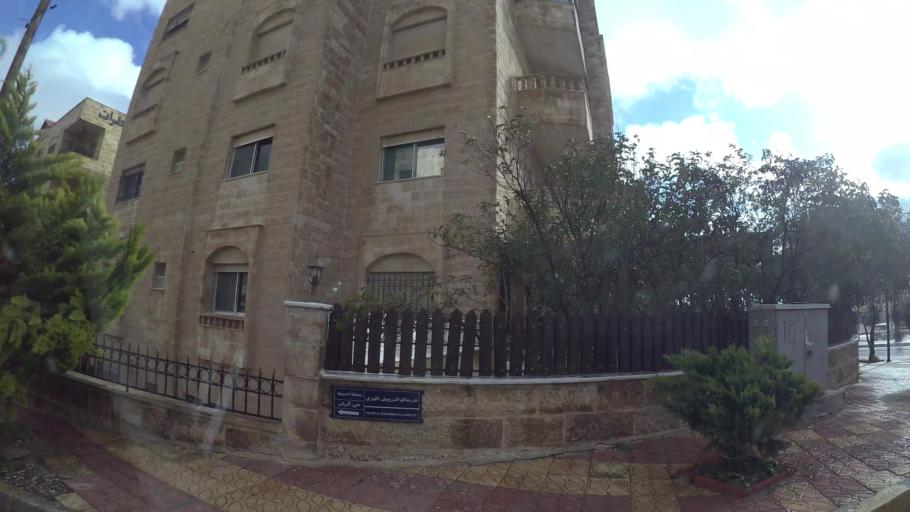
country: JO
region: Amman
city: Al Jubayhah
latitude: 32.0350
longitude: 35.8643
